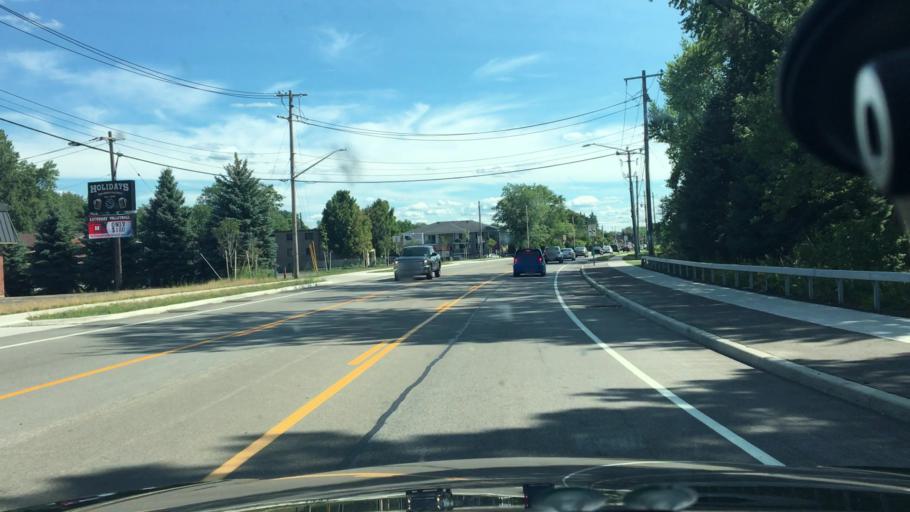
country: US
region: New York
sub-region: Erie County
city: West Seneca
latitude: 42.8688
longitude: -78.7873
